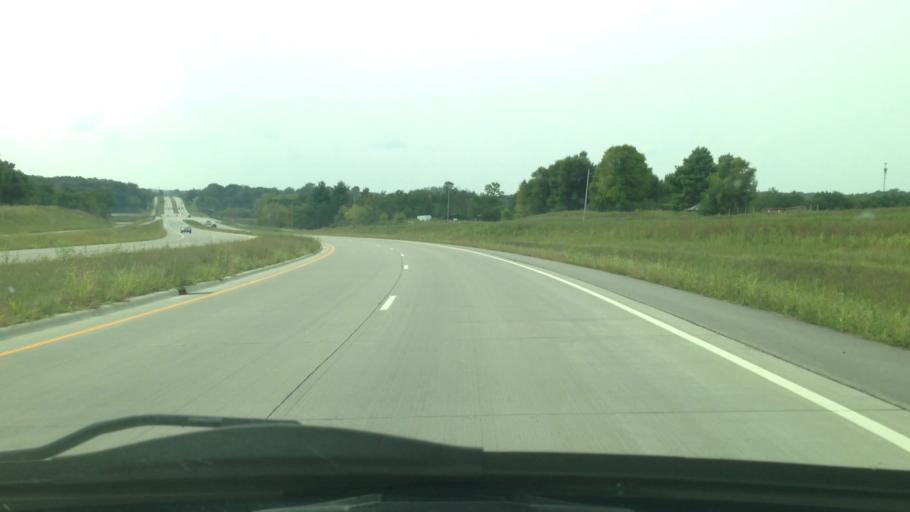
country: US
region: Minnesota
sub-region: Olmsted County
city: Rochester
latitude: 44.0793
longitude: -92.4629
